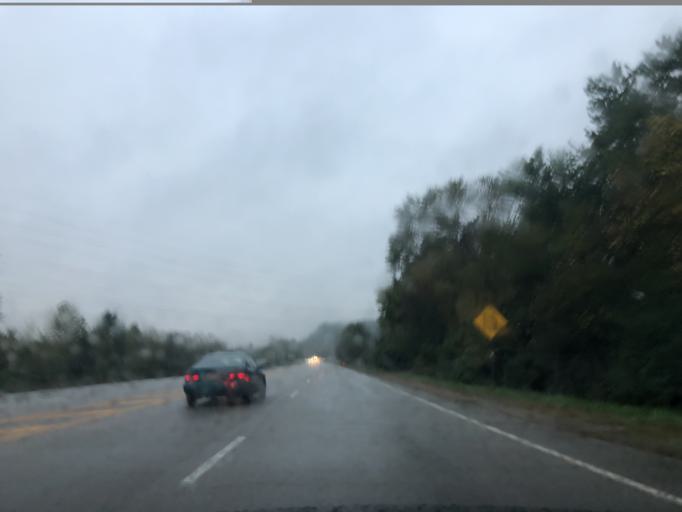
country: US
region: Ohio
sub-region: Hamilton County
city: The Village of Indian Hill
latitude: 39.2393
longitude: -84.3015
